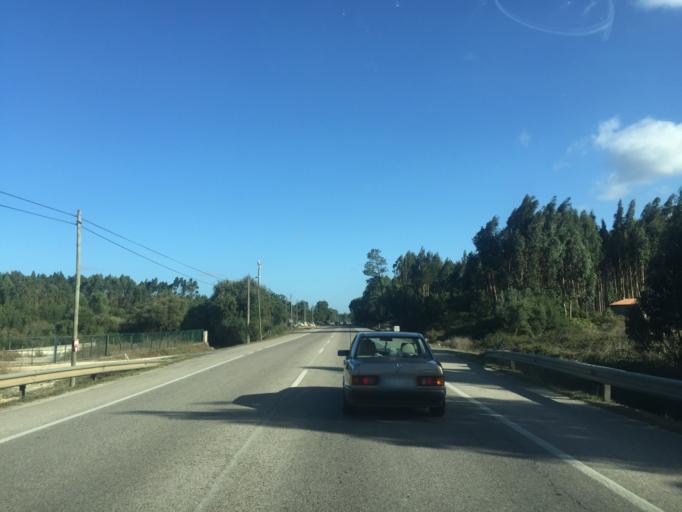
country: PT
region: Leiria
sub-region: Alcobaca
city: Turquel
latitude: 39.4979
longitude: -8.9294
